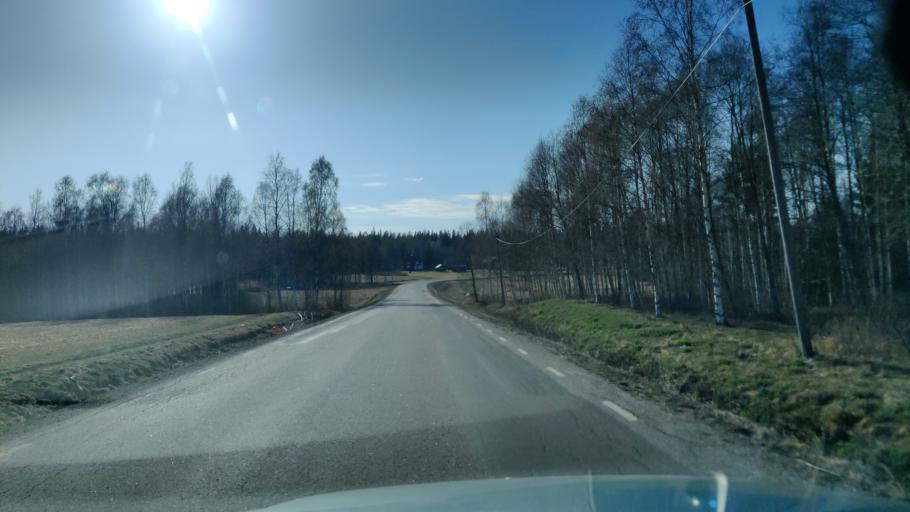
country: SE
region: Vaermland
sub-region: Munkfors Kommun
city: Munkfors
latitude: 59.9669
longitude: 13.4719
